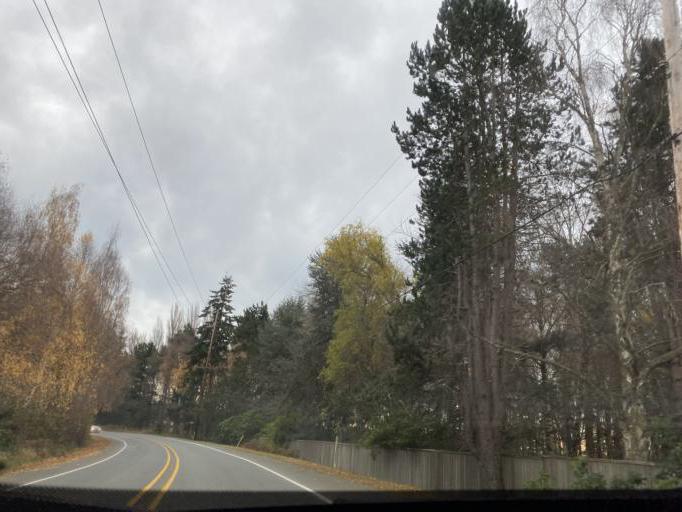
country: US
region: Washington
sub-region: Island County
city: Freeland
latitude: 48.0208
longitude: -122.5914
